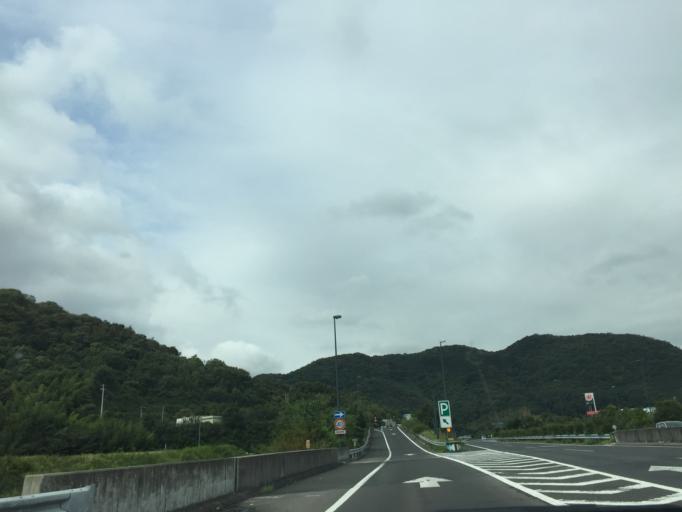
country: JP
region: Kagawa
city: Shido
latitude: 34.2761
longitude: 134.2674
